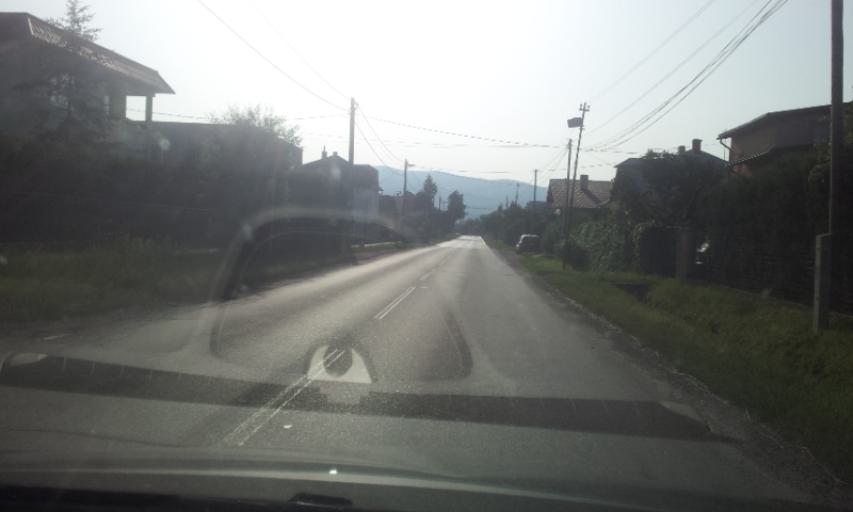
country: SK
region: Kosicky
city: Kosice
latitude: 48.6068
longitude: 21.3131
